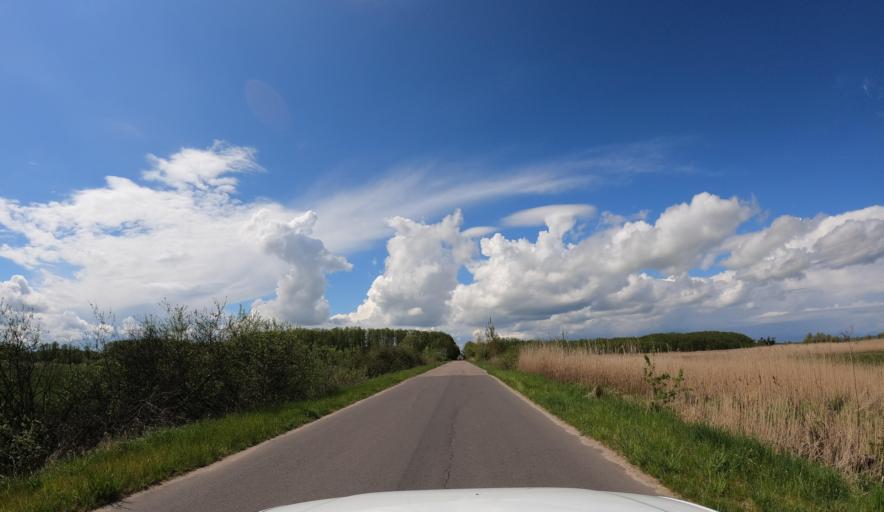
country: PL
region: West Pomeranian Voivodeship
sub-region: Powiat kamienski
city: Kamien Pomorski
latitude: 53.9153
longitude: 14.7017
